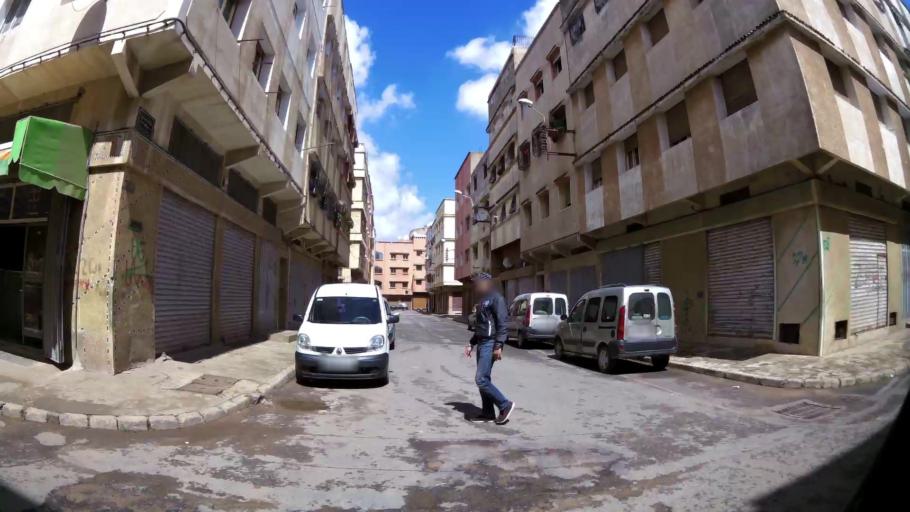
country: MA
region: Grand Casablanca
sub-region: Casablanca
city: Casablanca
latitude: 33.5368
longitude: -7.5711
